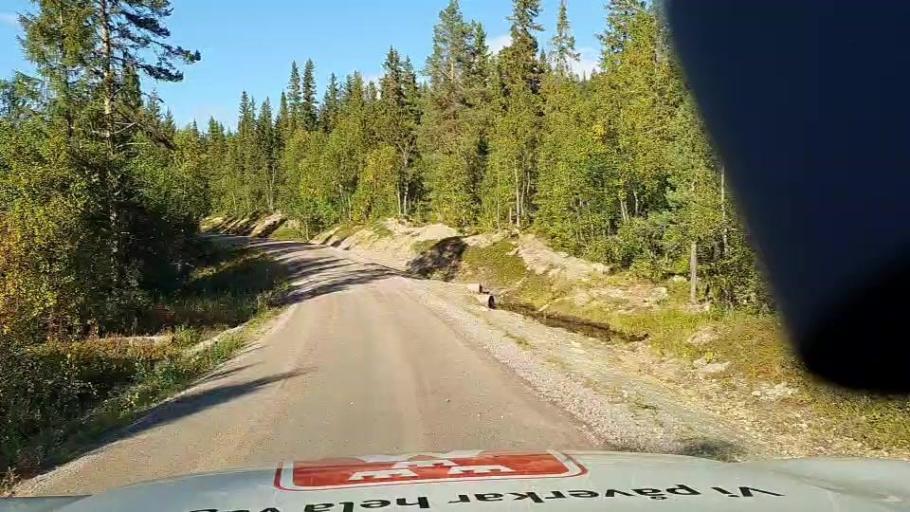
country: SE
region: Jaemtland
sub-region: Stroemsunds Kommun
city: Stroemsund
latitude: 64.5240
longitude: 15.1080
